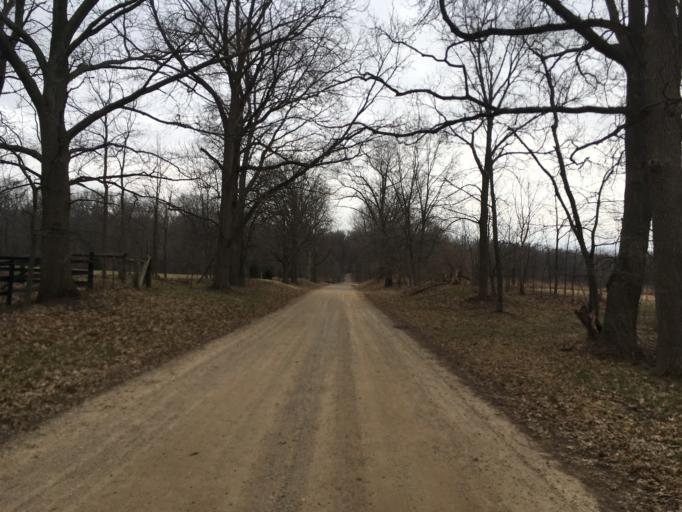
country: US
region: Michigan
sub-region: Jackson County
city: Grass Lake
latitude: 42.3255
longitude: -84.1950
